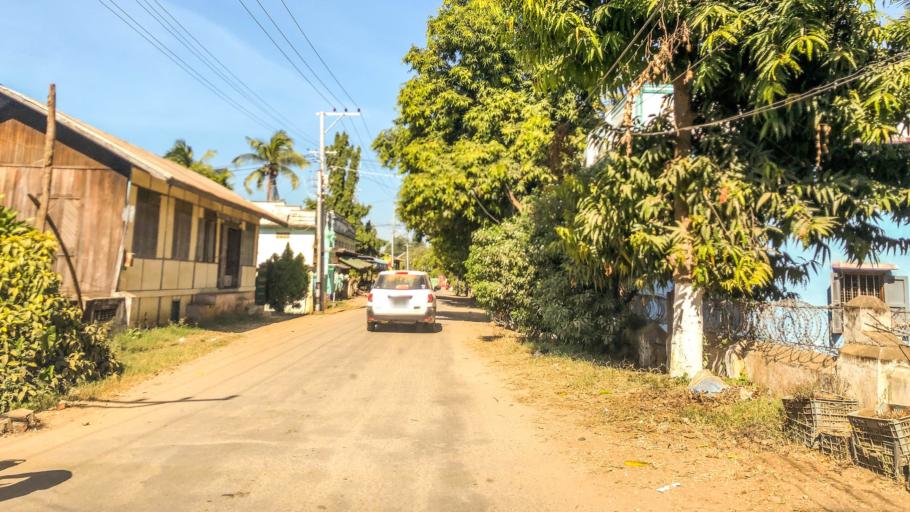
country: MM
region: Magway
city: Magway
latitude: 19.9687
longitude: 95.0446
